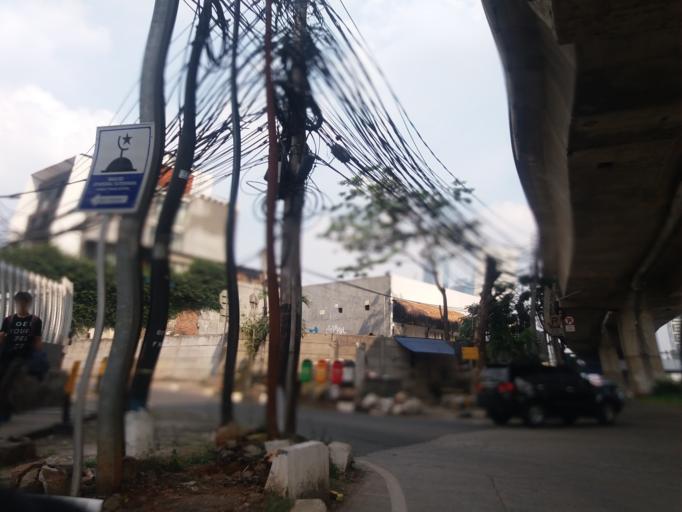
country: ID
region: Jakarta Raya
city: Jakarta
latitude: -6.2162
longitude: 106.8190
